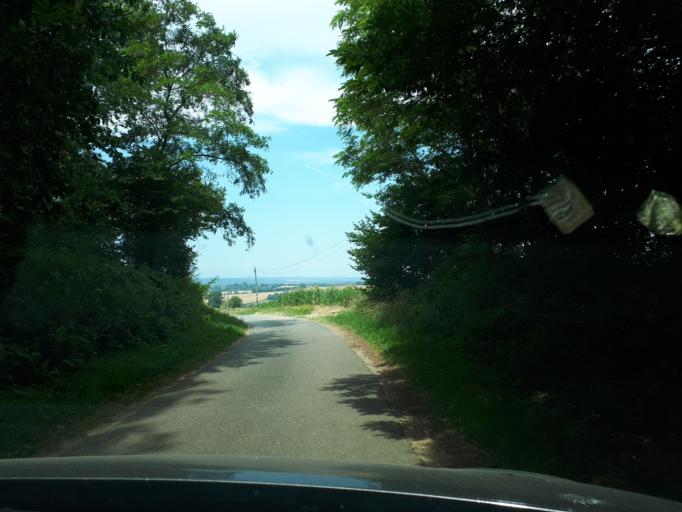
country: FR
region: Centre
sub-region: Departement du Cher
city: Sancerre
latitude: 47.3112
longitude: 2.7405
